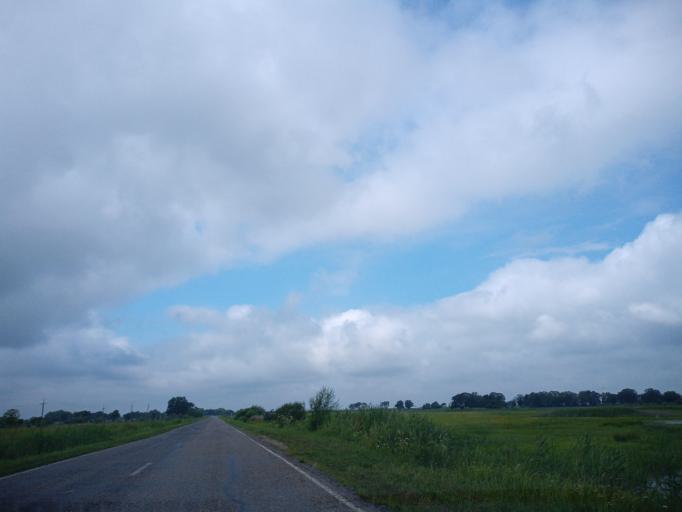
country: RU
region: Primorskiy
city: Dal'nerechensk
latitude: 45.9368
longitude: 133.8612
